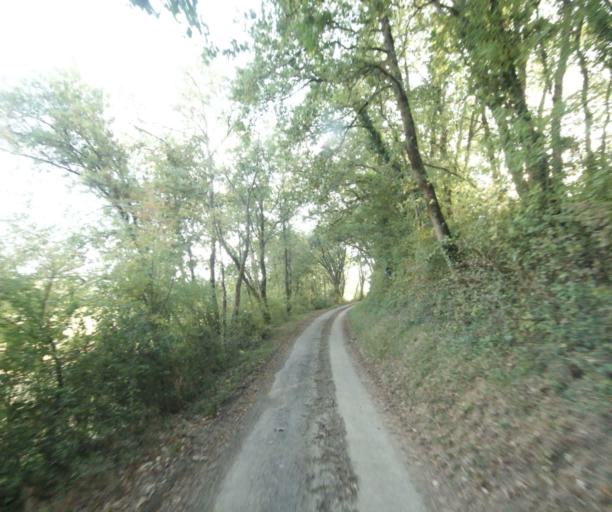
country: FR
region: Midi-Pyrenees
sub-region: Departement du Gers
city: Gondrin
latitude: 43.9037
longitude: 0.2895
